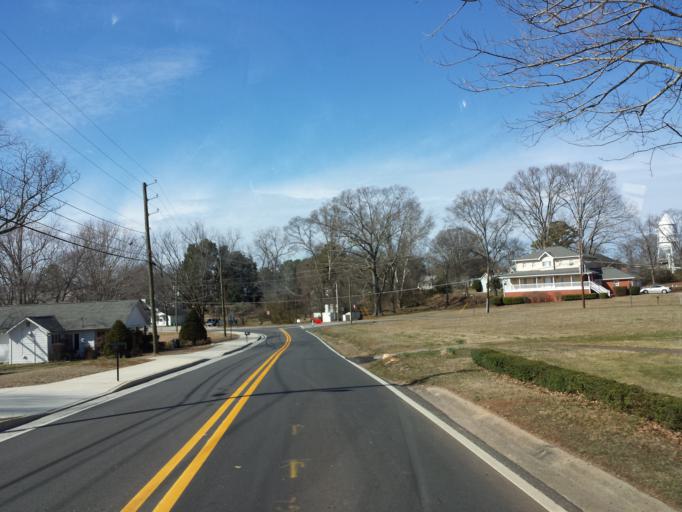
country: US
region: Georgia
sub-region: Cobb County
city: Kennesaw
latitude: 34.0220
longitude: -84.6121
